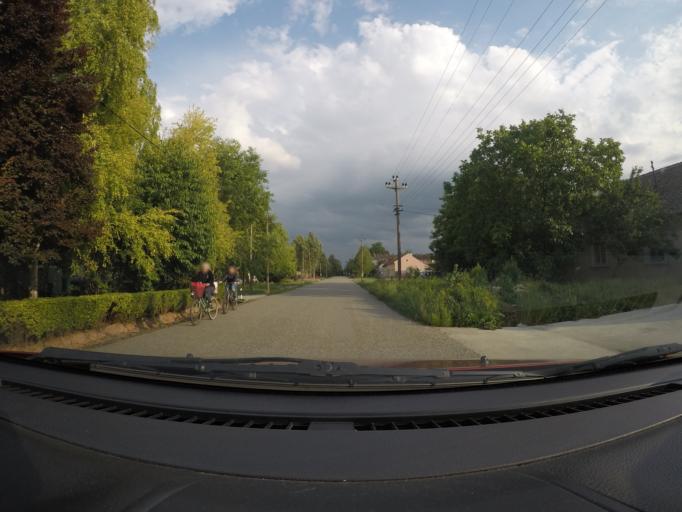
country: RS
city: Debeljaca
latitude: 45.0714
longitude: 20.6008
